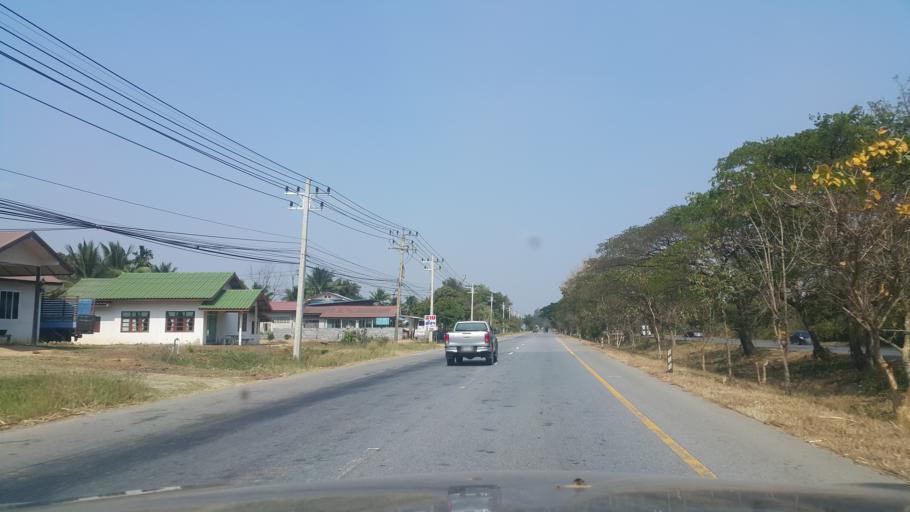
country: TH
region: Nakhon Ratchasima
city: Wang Nam Khiao
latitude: 14.5162
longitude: 101.9601
